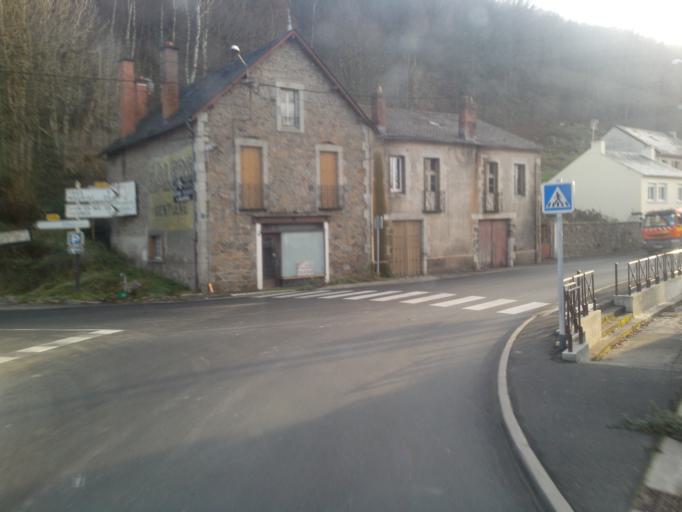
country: FR
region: Limousin
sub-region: Departement de la Correze
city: Bort-les-Orgues
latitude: 45.3806
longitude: 2.4867
